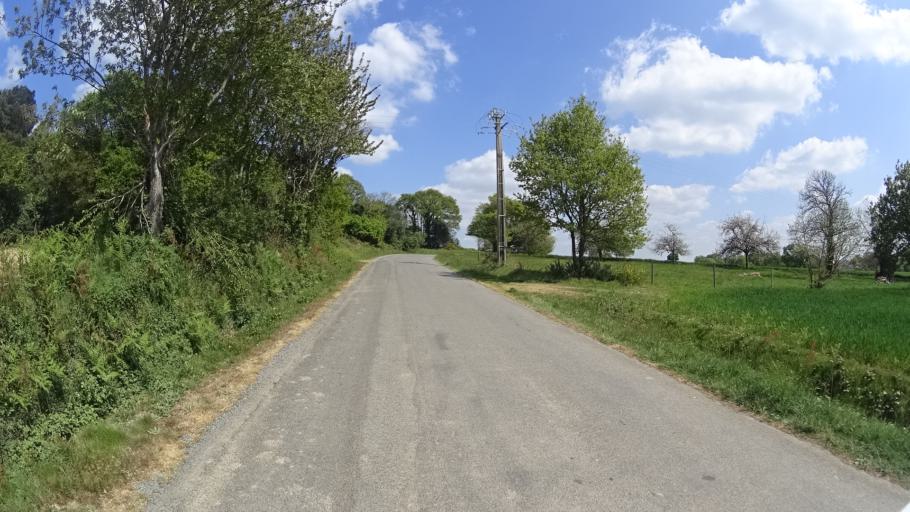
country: FR
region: Brittany
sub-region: Departement du Morbihan
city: Allaire
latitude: 47.5987
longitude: -2.1529
